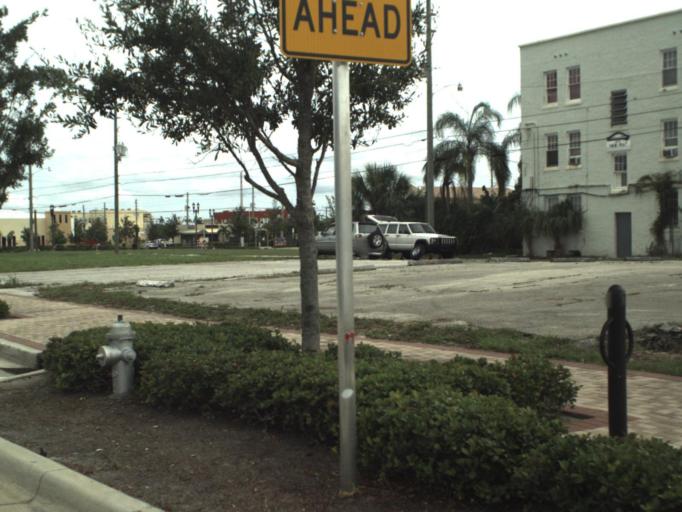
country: US
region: Florida
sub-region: Palm Beach County
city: West Palm Beach
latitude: 26.7363
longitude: -80.0562
